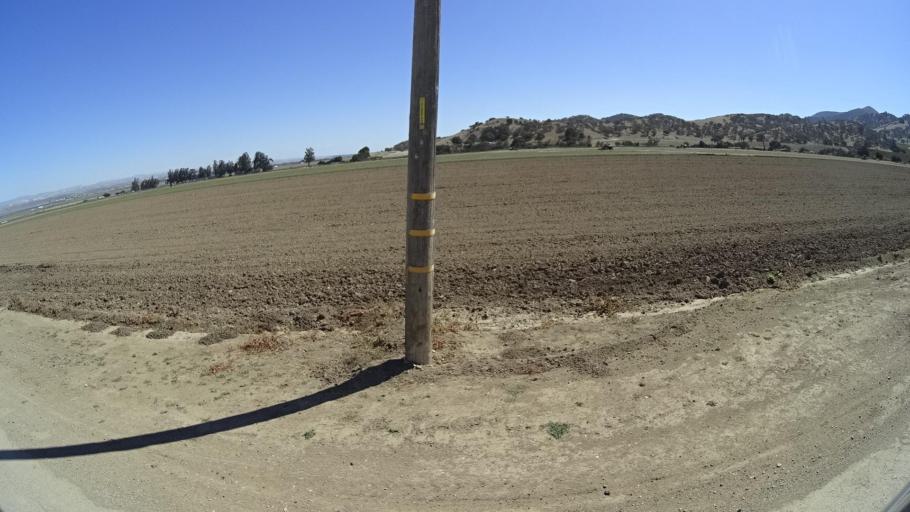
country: US
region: California
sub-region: Monterey County
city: King City
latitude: 36.2287
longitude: -121.1834
